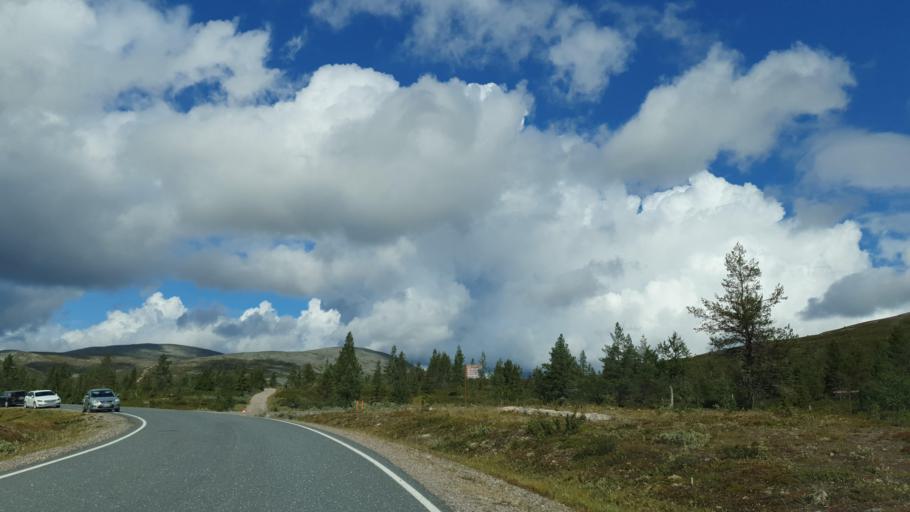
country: FI
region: Lapland
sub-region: Tunturi-Lappi
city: Muonio
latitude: 68.0442
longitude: 24.0683
